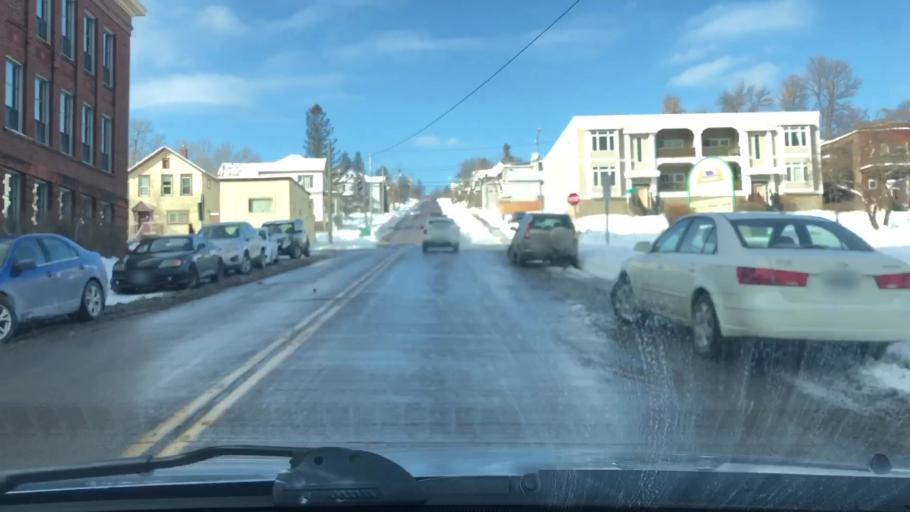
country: US
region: Minnesota
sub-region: Saint Louis County
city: Duluth
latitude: 46.7893
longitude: -92.1020
